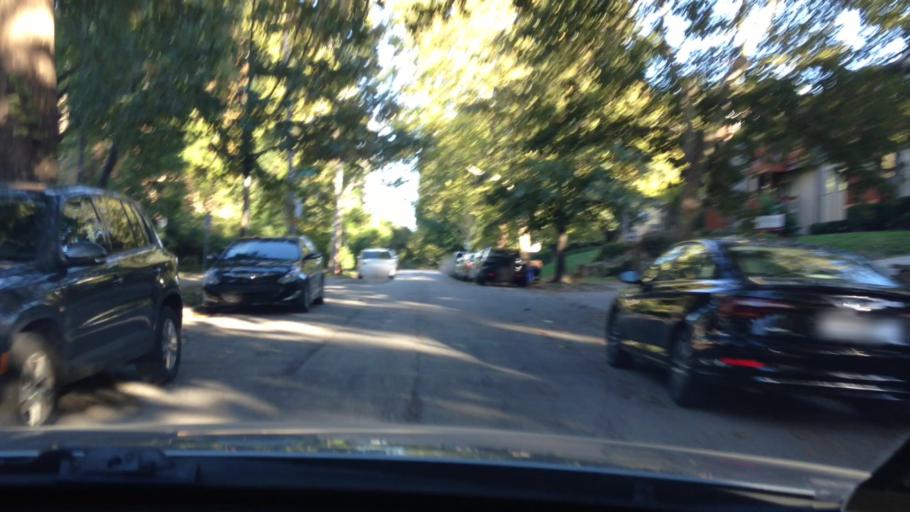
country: US
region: Kansas
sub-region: Johnson County
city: Westwood
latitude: 39.0583
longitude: -94.5995
